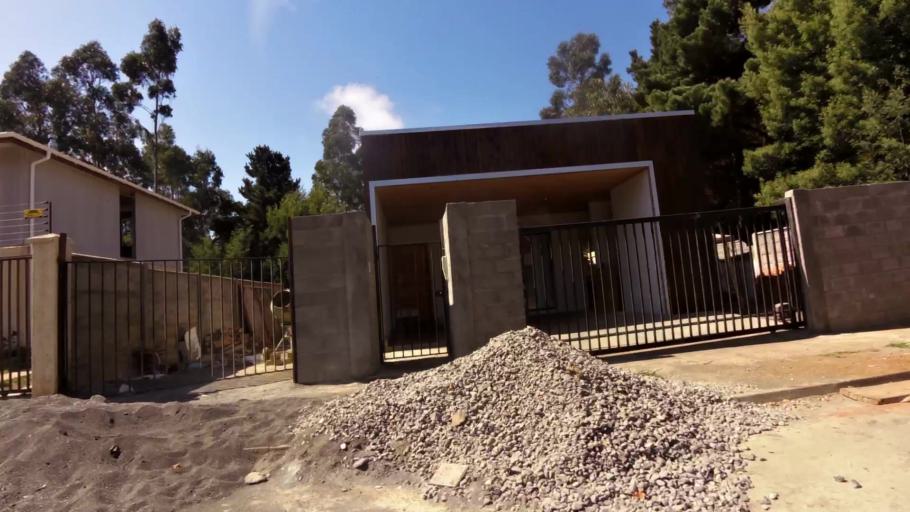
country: CL
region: Biobio
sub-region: Provincia de Concepcion
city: Concepcion
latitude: -36.7837
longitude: -73.0491
